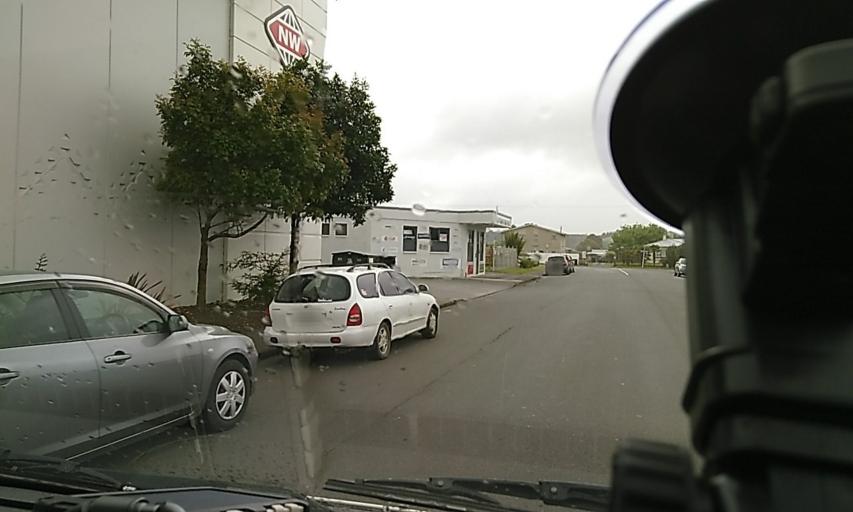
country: NZ
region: Northland
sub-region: Far North District
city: Waimate North
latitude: -35.4094
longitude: 173.8012
